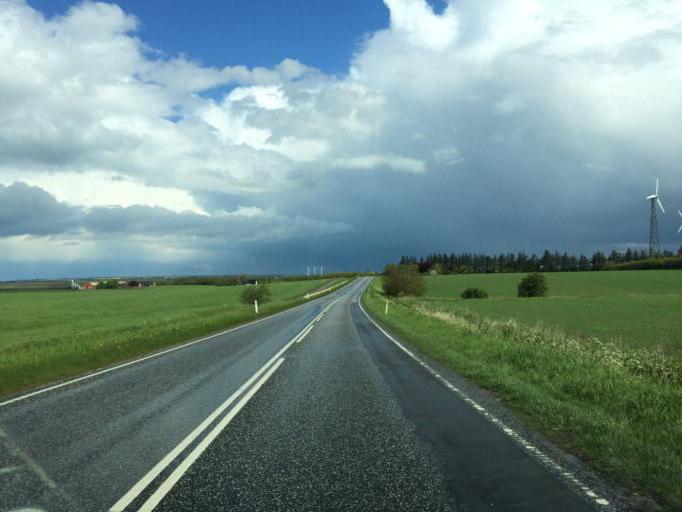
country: DK
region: Central Jutland
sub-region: Holstebro Kommune
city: Vinderup
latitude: 56.4600
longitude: 8.7672
